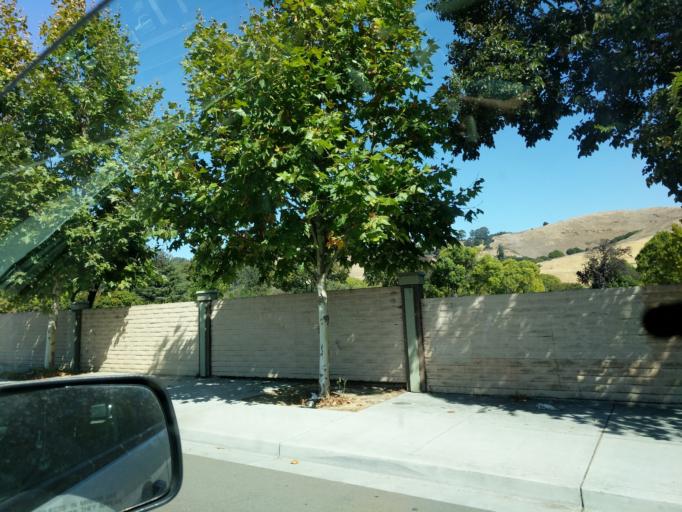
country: US
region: California
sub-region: Alameda County
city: Hayward
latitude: 37.6462
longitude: -122.0629
